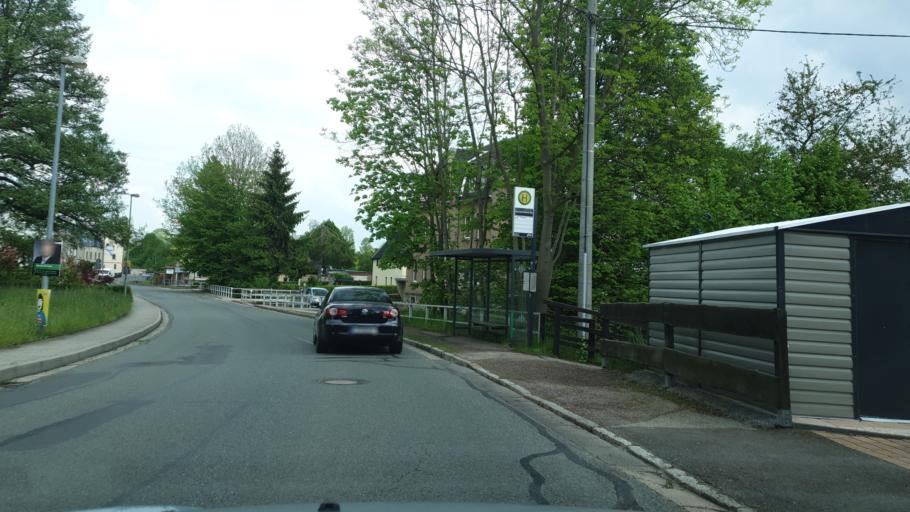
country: DE
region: Saxony
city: Wittgensdorf
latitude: 50.8610
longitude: 12.8431
